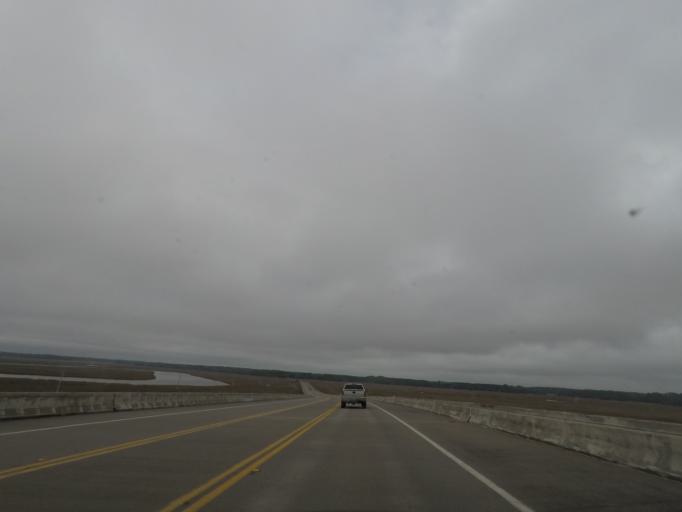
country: US
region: South Carolina
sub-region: Charleston County
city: Meggett
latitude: 32.6387
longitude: -80.3402
